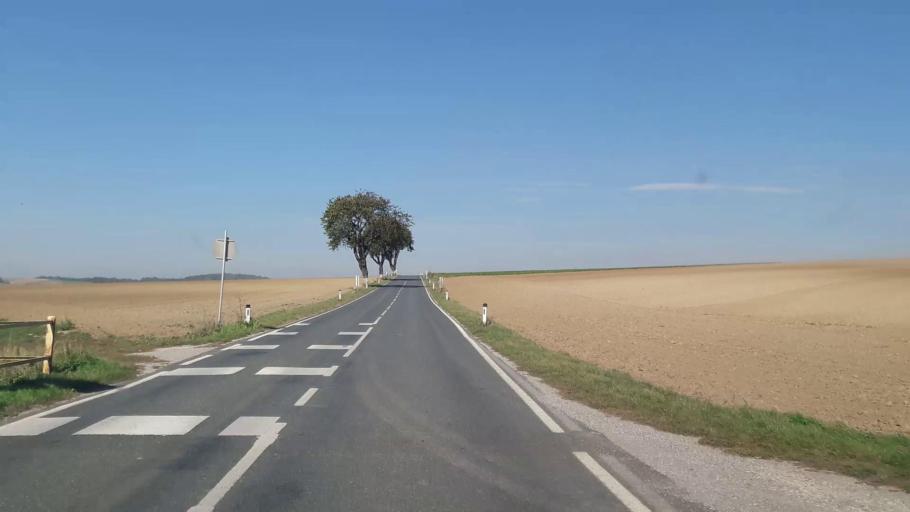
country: AT
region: Lower Austria
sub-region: Politischer Bezirk Korneuburg
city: Ernstbrunn
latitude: 48.5041
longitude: 16.3629
